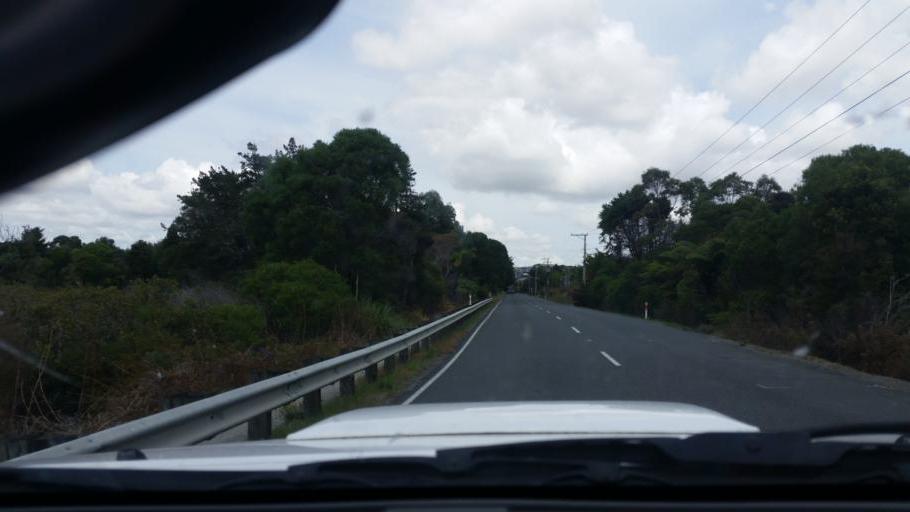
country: NZ
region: Auckland
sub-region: Auckland
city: Wellsford
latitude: -36.1185
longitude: 174.5732
